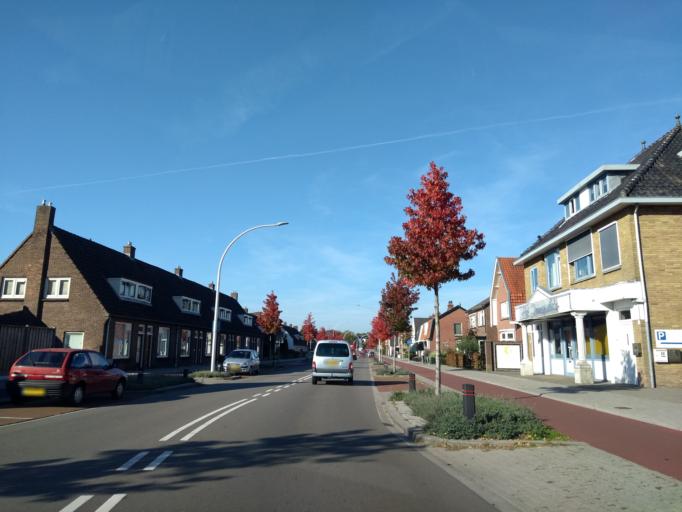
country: NL
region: Overijssel
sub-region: Gemeente Hengelo
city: Hengelo
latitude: 52.2586
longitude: 6.7764
